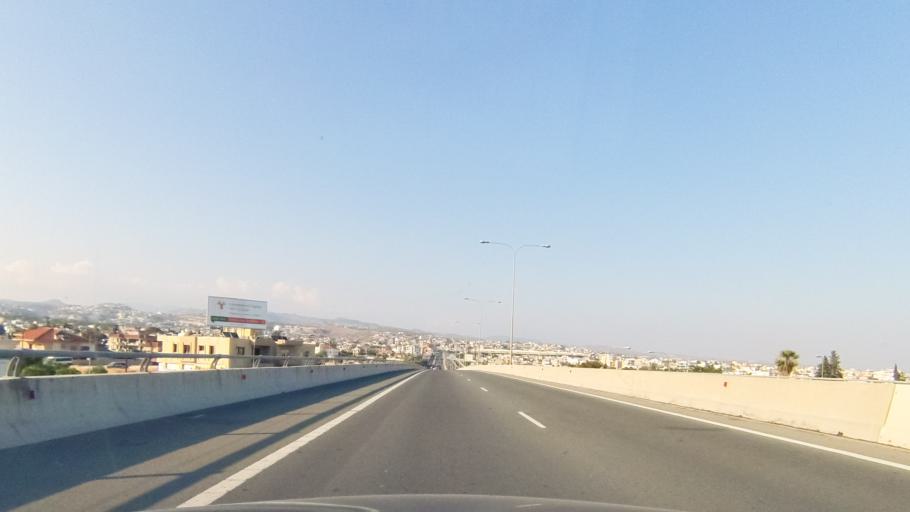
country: CY
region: Limassol
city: Pano Polemidia
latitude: 34.6939
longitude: 33.0133
